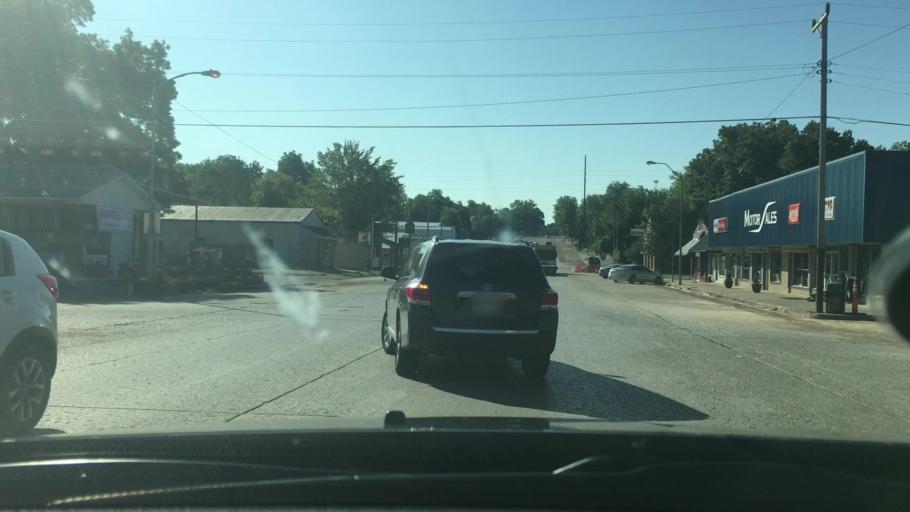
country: US
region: Oklahoma
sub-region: Johnston County
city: Tishomingo
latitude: 34.2348
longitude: -96.6775
